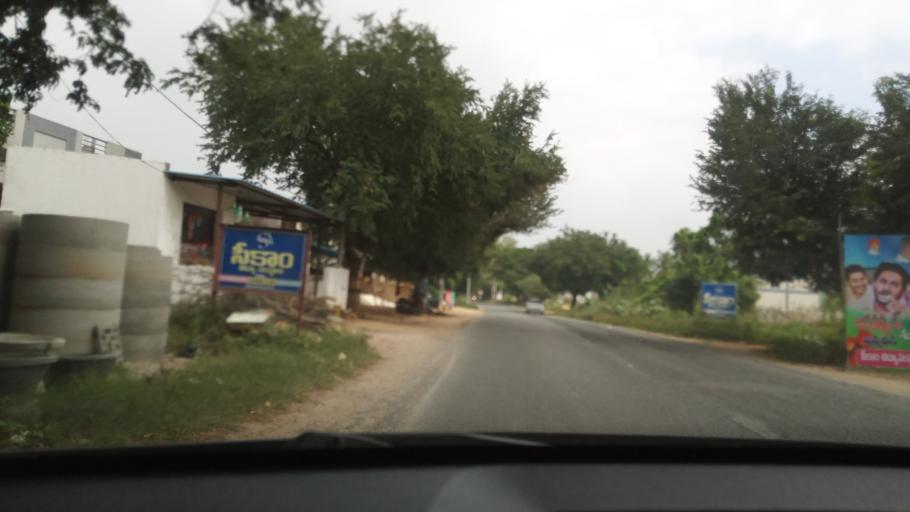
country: IN
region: Andhra Pradesh
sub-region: Chittoor
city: Madanapalle
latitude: 13.6517
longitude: 78.8172
